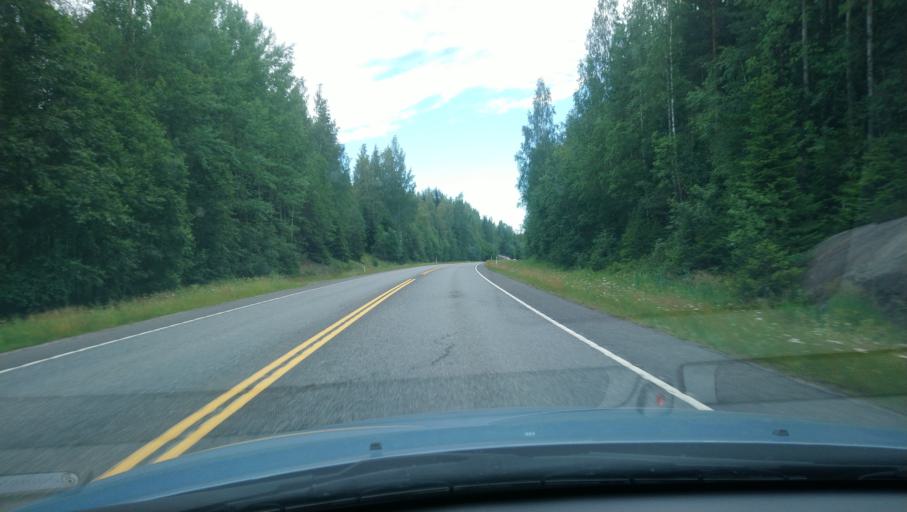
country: FI
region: Uusimaa
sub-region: Porvoo
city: Askola
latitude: 60.4365
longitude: 25.5752
